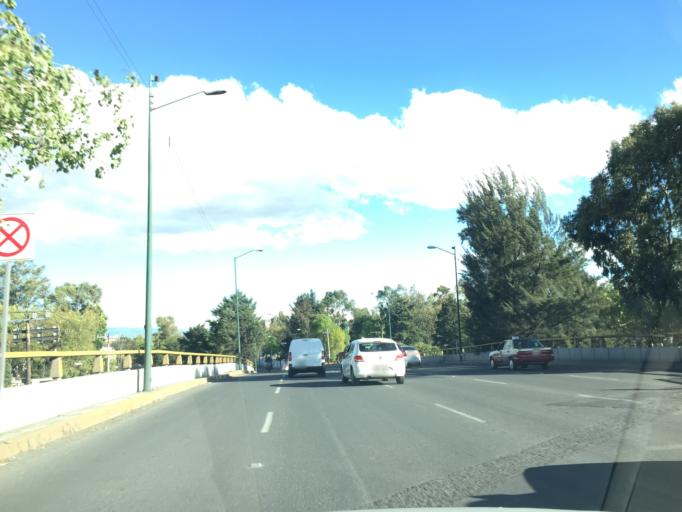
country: MX
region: Mexico
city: Colonia Lindavista
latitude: 19.4868
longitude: -99.1435
